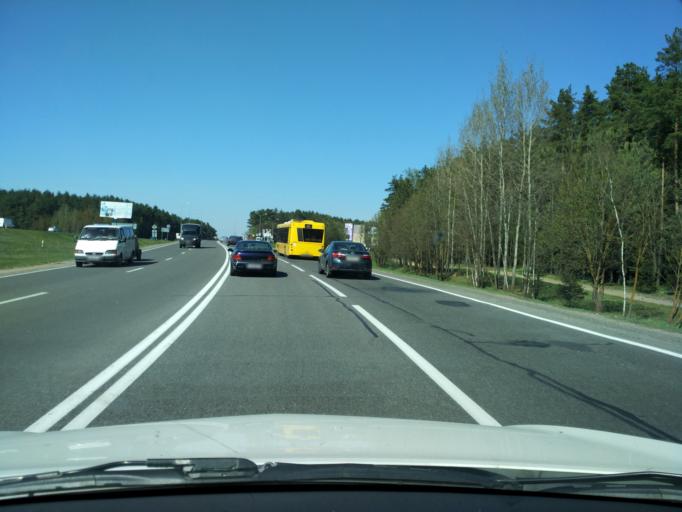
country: BY
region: Minsk
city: Borovlyany
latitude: 53.9795
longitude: 27.6549
